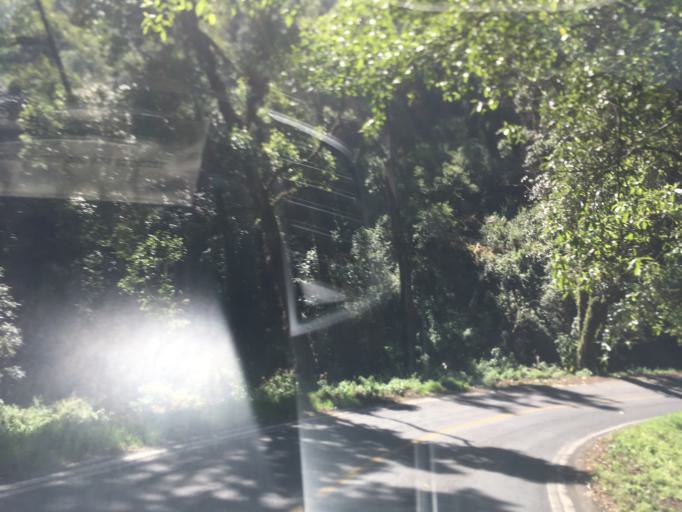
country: MX
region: Michoacan
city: Tzitzio
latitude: 19.6696
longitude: -100.8034
